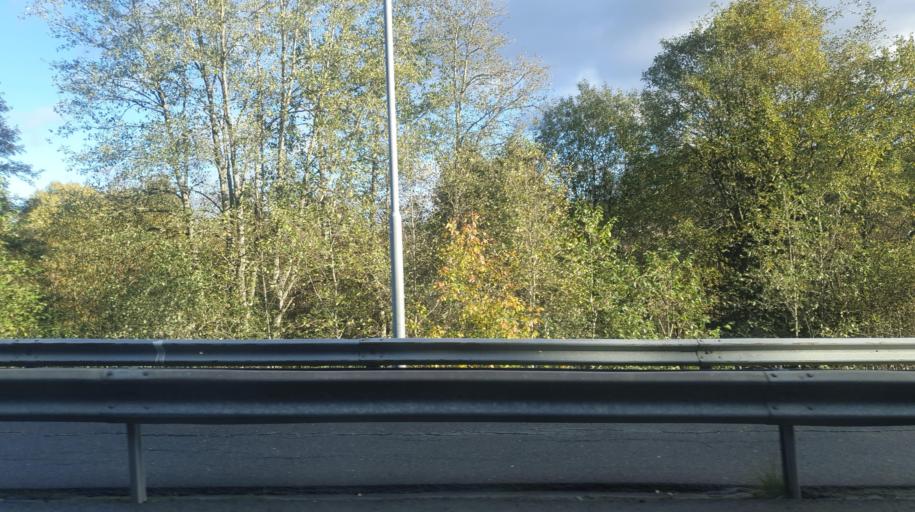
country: NO
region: Sor-Trondelag
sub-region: Klaebu
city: Klaebu
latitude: 63.3033
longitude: 10.4645
